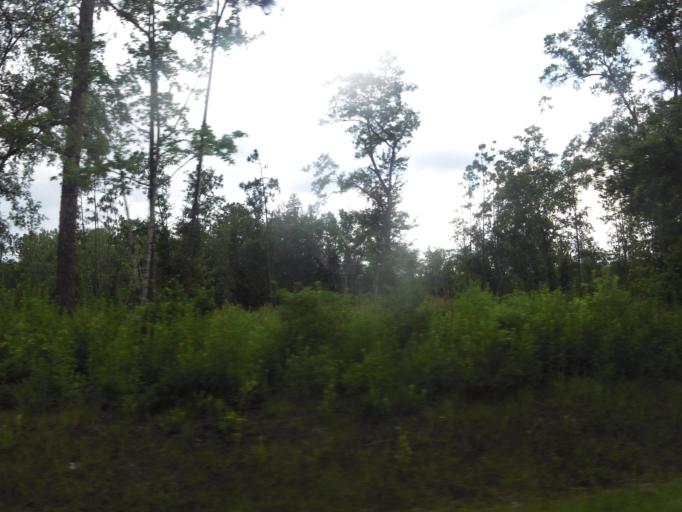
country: US
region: Florida
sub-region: Duval County
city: Baldwin
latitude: 30.3284
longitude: -81.8727
